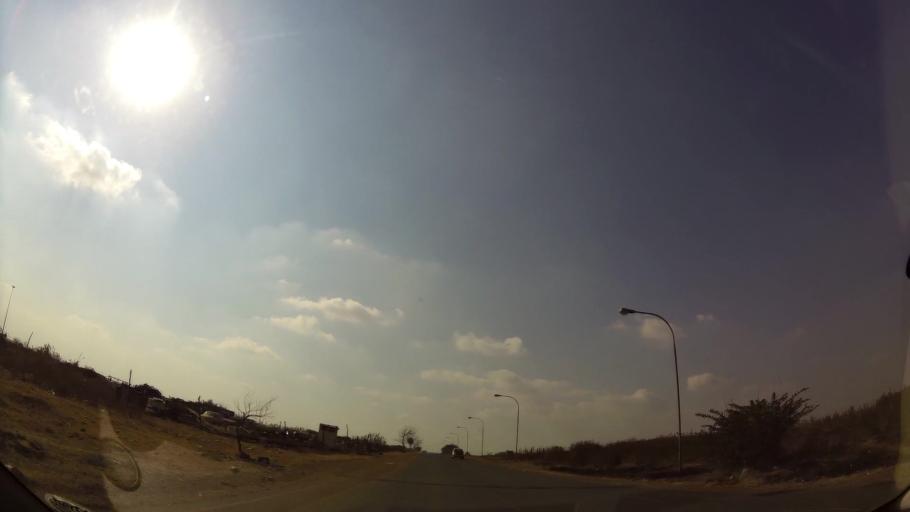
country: ZA
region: Gauteng
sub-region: Ekurhuleni Metropolitan Municipality
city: Springs
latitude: -26.1335
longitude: 28.4779
